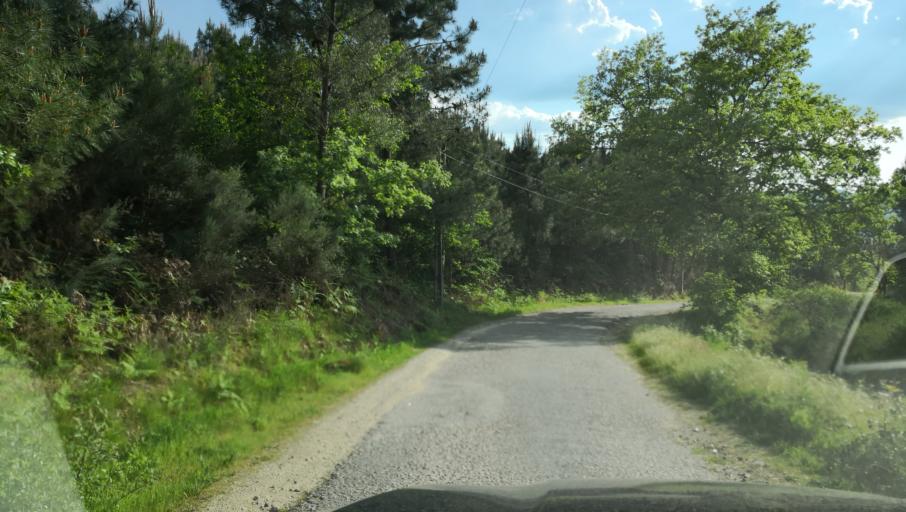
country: PT
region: Vila Real
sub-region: Vila Real
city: Vila Real
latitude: 41.2948
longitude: -7.6974
